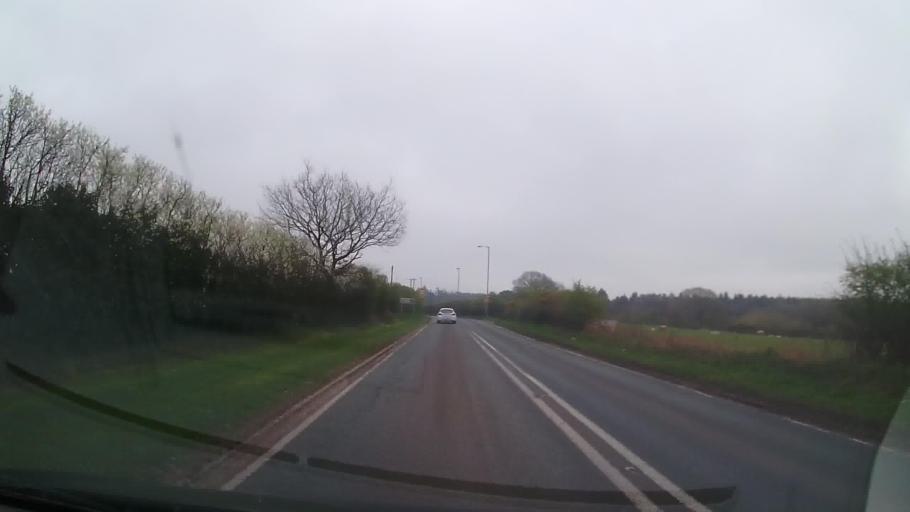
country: GB
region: England
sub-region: Shropshire
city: Market Drayton
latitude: 52.9201
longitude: -2.3983
